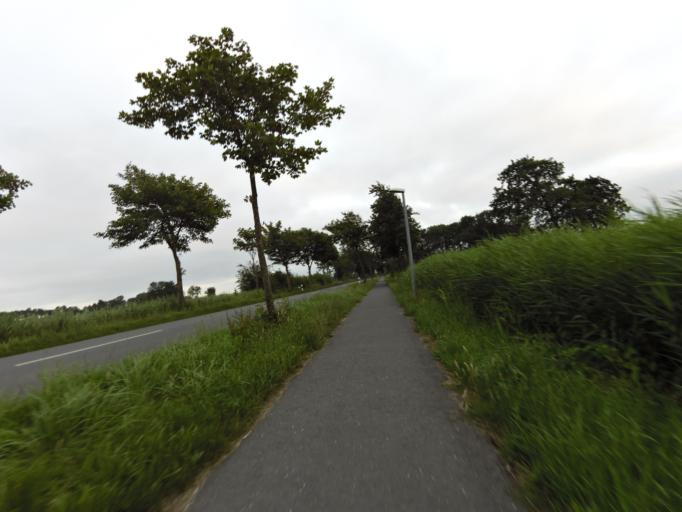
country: DE
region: Lower Saxony
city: Padingbuttel
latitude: 53.7162
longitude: 8.5485
